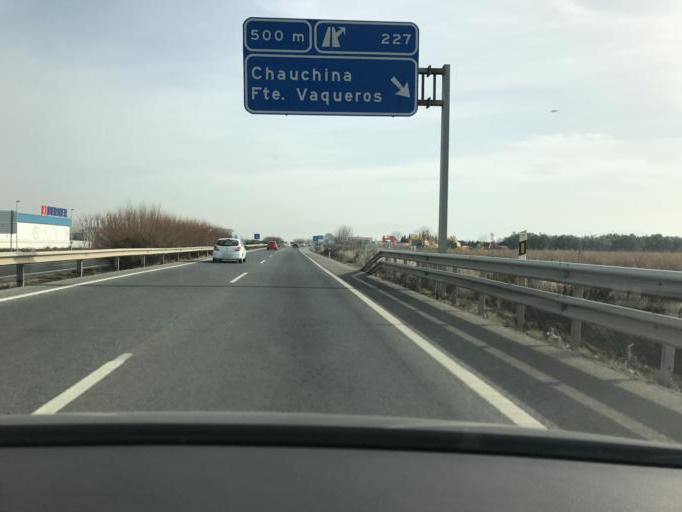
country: ES
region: Andalusia
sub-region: Provincia de Granada
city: Chauchina
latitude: 37.1920
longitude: -3.7881
